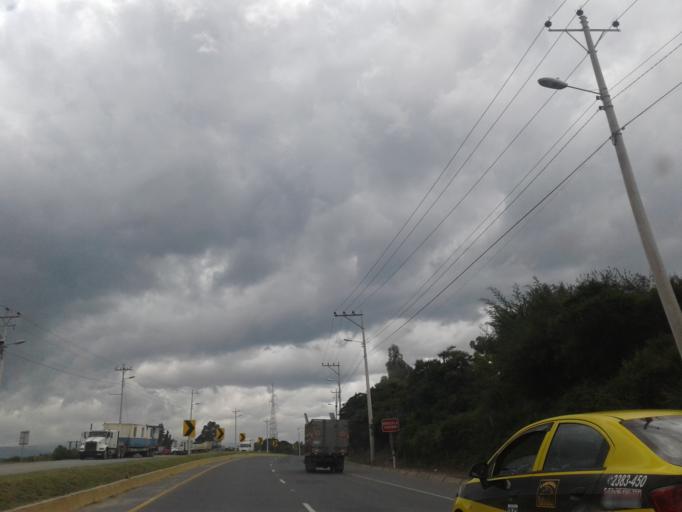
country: EC
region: Pichincha
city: Sangolqui
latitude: -0.3095
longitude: -78.3646
